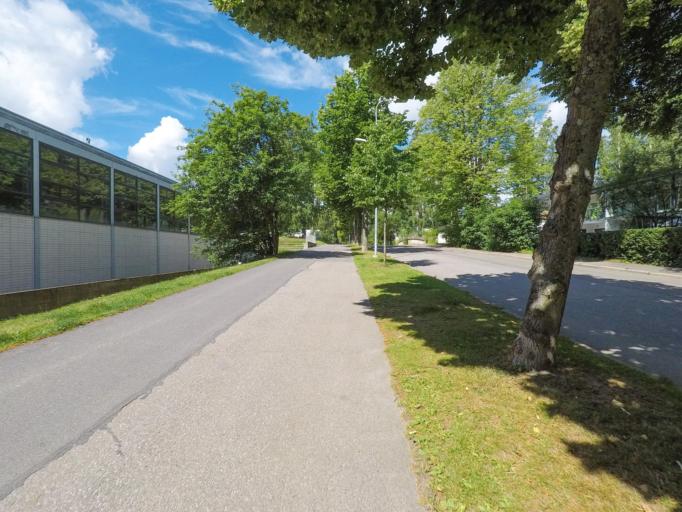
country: FI
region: Uusimaa
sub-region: Helsinki
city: Vantaa
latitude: 60.2186
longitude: 25.0931
